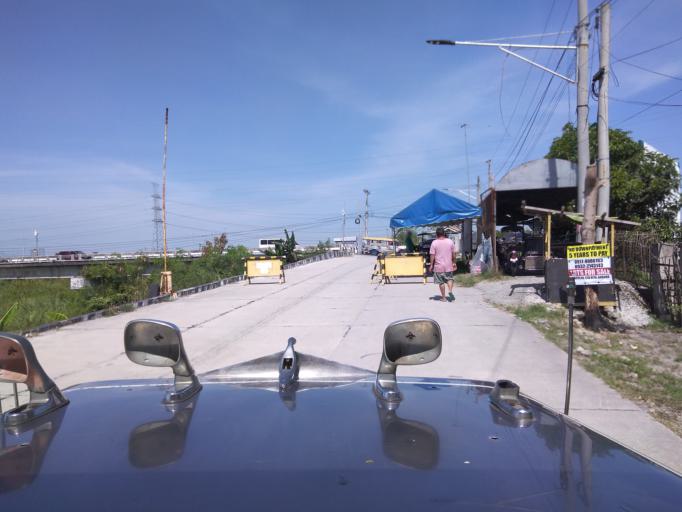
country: PH
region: Central Luzon
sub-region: Province of Pampanga
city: Bacolor
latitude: 15.0070
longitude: 120.6589
